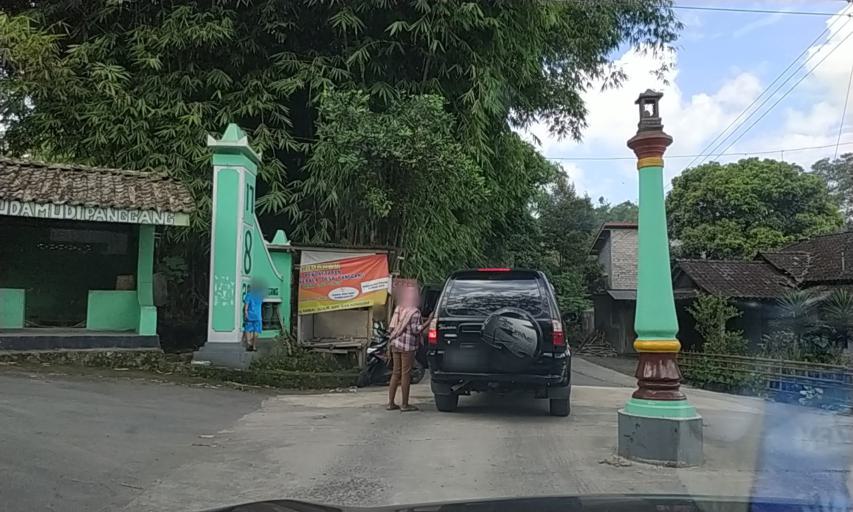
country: ID
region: Central Java
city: Jogonalan
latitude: -7.6288
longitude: 110.4707
